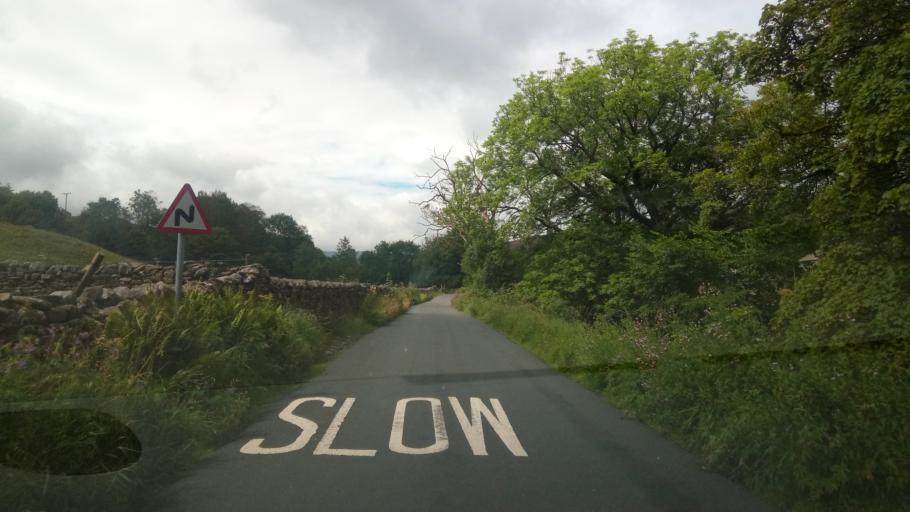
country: GB
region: England
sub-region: North Yorkshire
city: Ingleton
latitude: 54.2768
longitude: -2.3673
